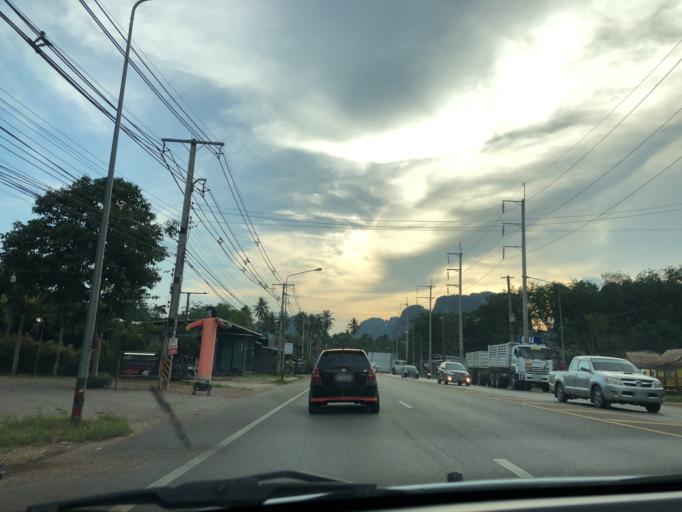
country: TH
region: Krabi
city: Krabi
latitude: 8.0806
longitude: 98.8713
